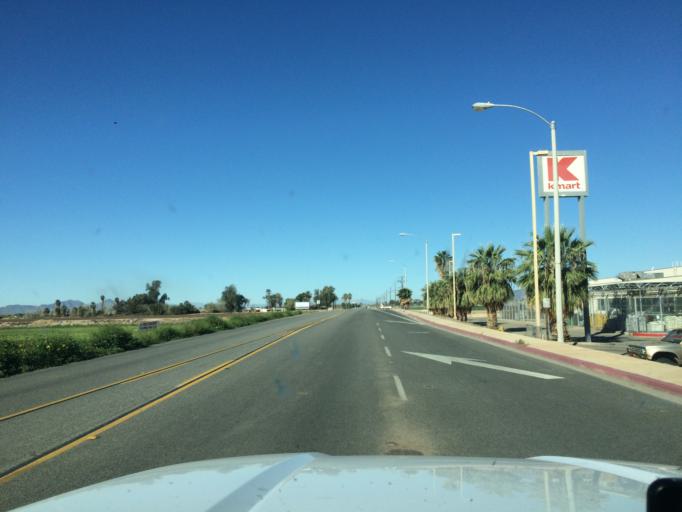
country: US
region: California
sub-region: Riverside County
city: Blythe
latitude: 33.6102
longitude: -114.6125
